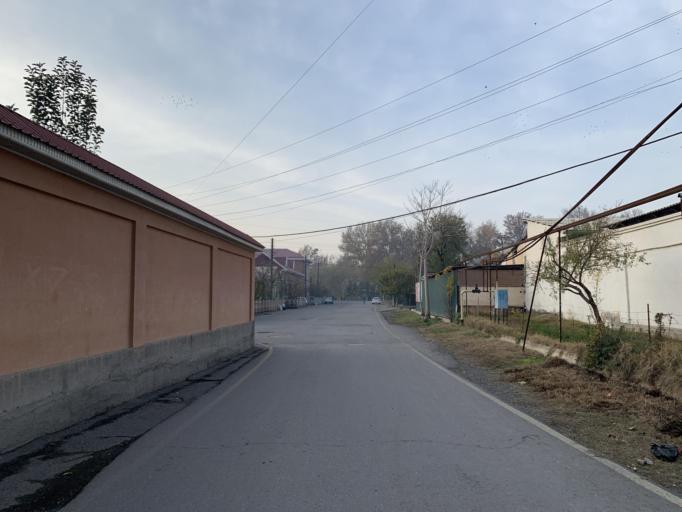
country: UZ
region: Fergana
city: Qo`qon
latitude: 40.5427
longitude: 70.9264
